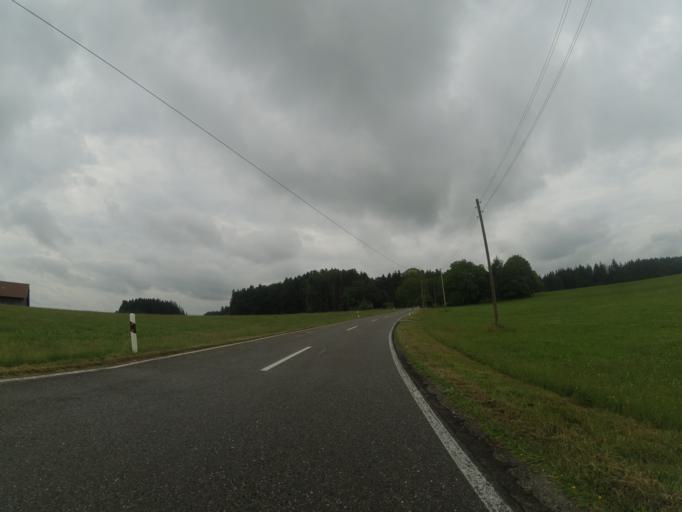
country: DE
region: Baden-Wuerttemberg
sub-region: Tuebingen Region
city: Wangen im Allgau
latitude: 47.7380
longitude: 9.8450
